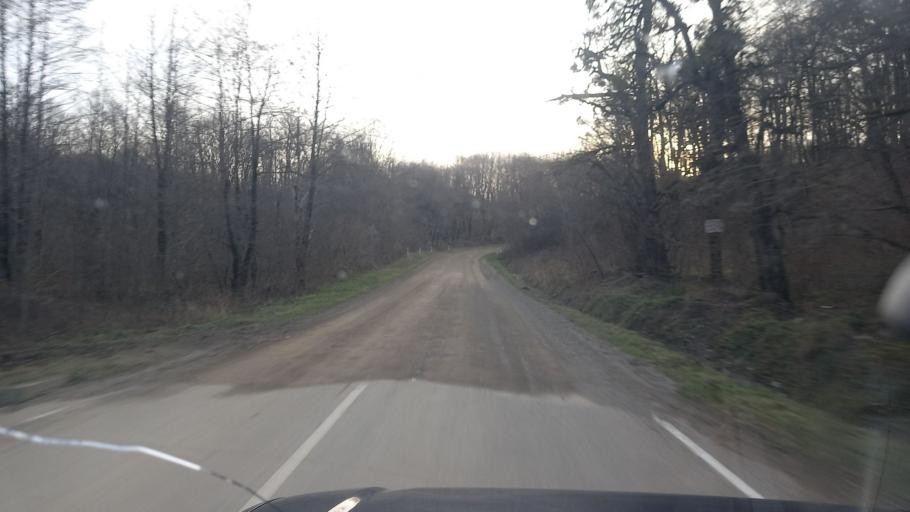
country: RU
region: Krasnodarskiy
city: Khadyzhensk
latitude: 44.3381
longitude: 39.2805
